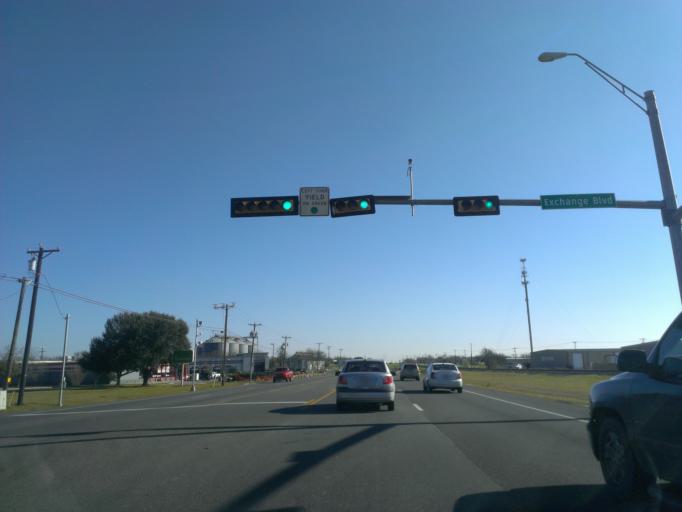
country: US
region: Texas
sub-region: Williamson County
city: Hutto
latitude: 30.5414
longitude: -97.5554
